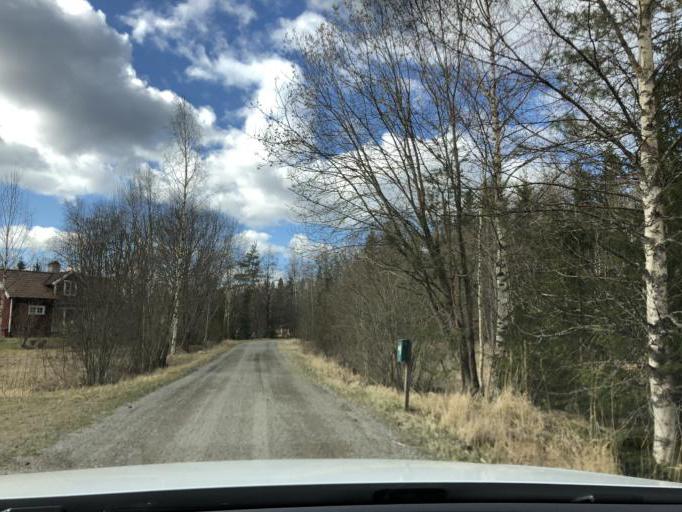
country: SE
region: Uppsala
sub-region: Tierps Kommun
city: Tierp
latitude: 60.3280
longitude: 17.3557
